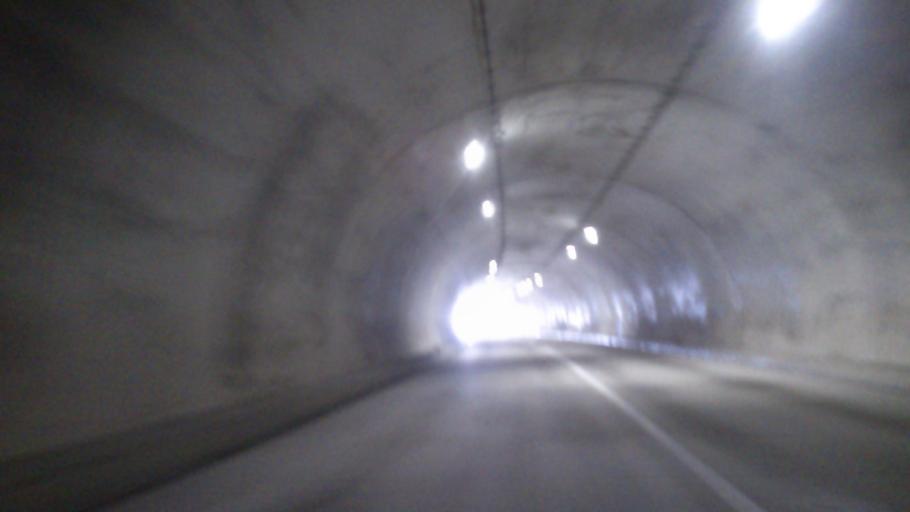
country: JP
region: Aomori
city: Hirosaki
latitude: 40.5334
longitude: 140.2532
